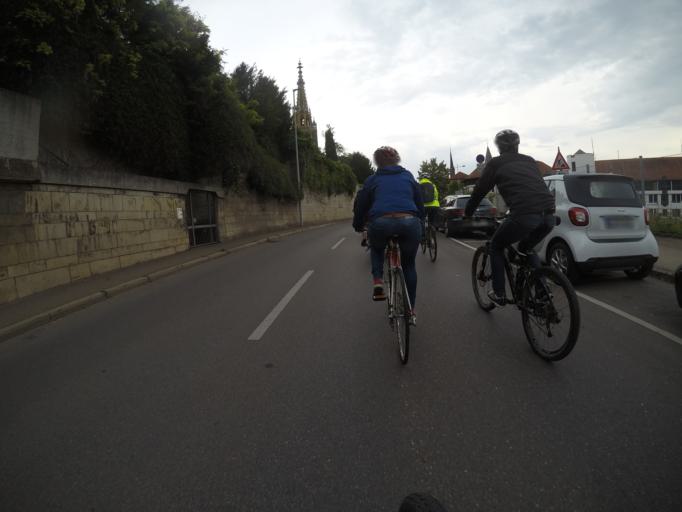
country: DE
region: Baden-Wuerttemberg
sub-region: Regierungsbezirk Stuttgart
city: Esslingen
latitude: 48.7436
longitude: 9.3031
